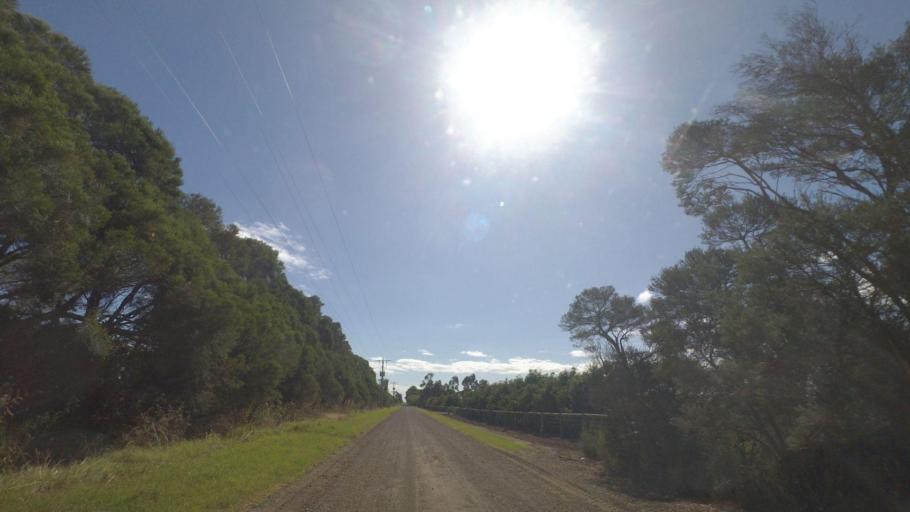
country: AU
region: Victoria
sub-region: Cardinia
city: Pakenham South
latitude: -38.1384
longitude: 145.4792
